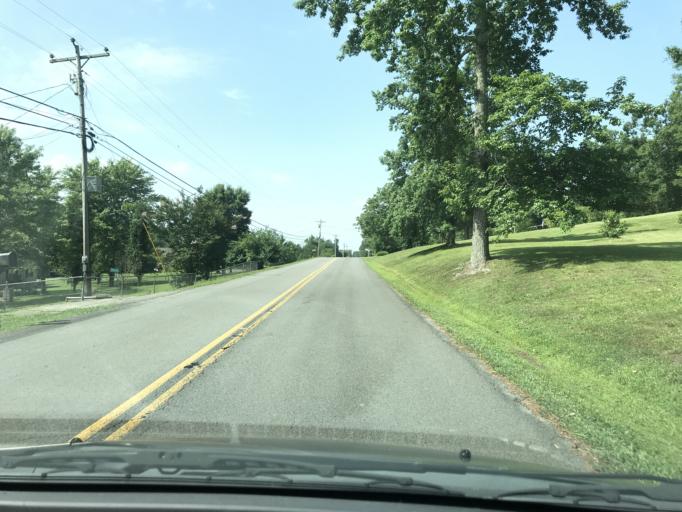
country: US
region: Tennessee
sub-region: Hamilton County
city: Apison
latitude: 35.0617
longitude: -84.9820
